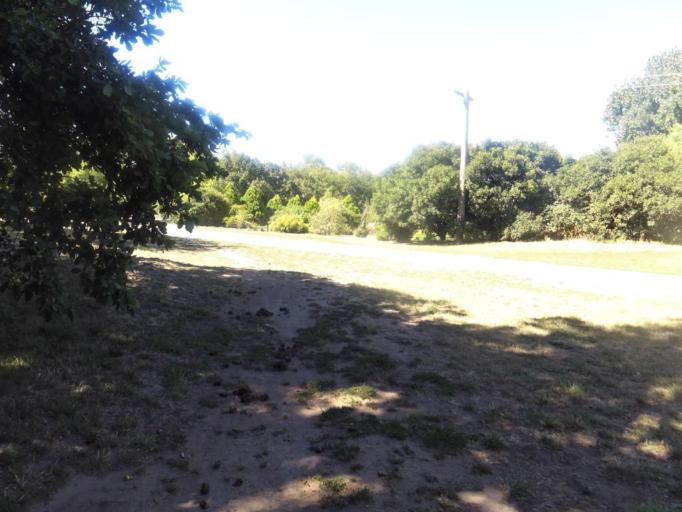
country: AU
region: Victoria
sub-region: Mount Alexander
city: Castlemaine
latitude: -37.2402
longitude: 144.4418
